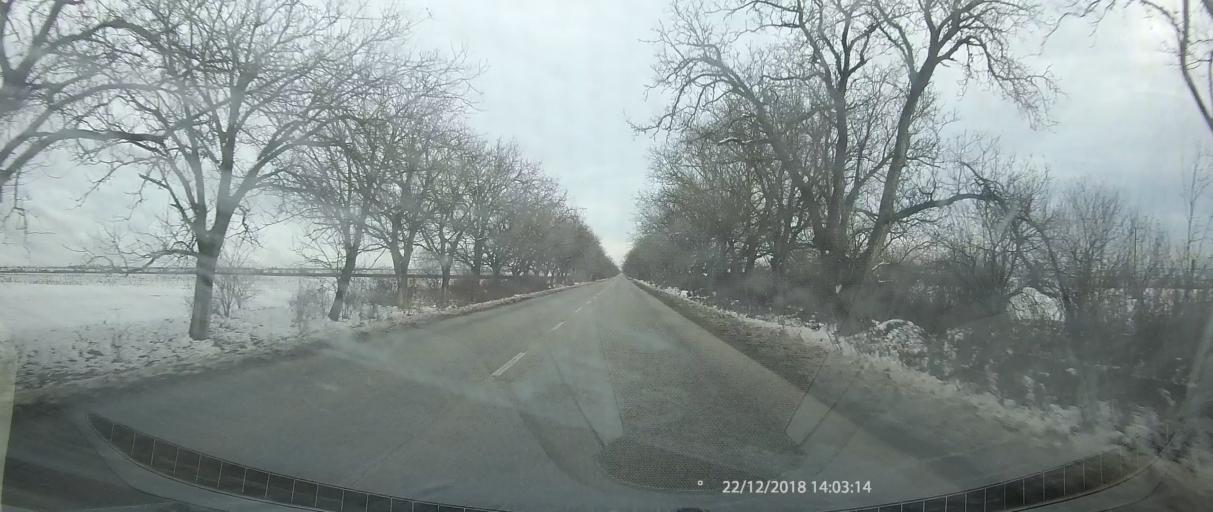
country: BG
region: Pleven
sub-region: Obshtina Dolni Dubnik
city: Dolni Dubnik
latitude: 43.3900
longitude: 24.4008
